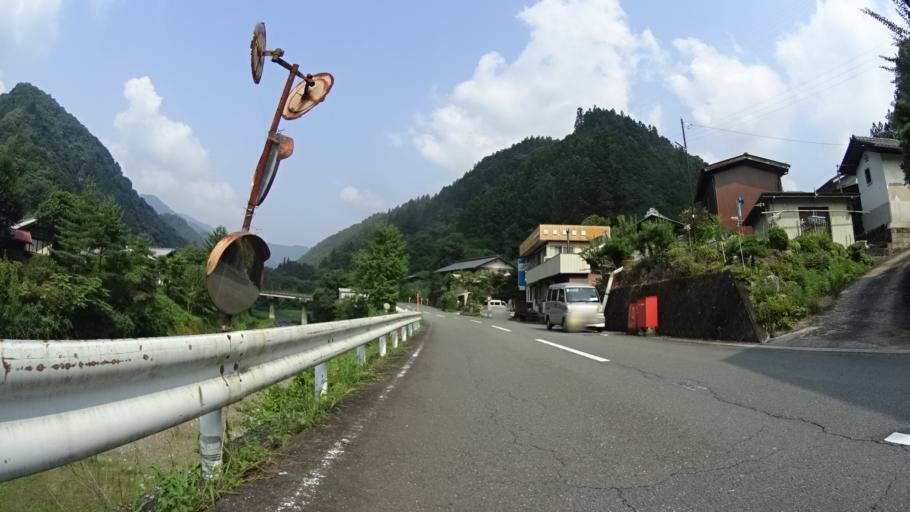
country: JP
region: Saitama
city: Chichibu
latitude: 36.0483
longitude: 138.8871
